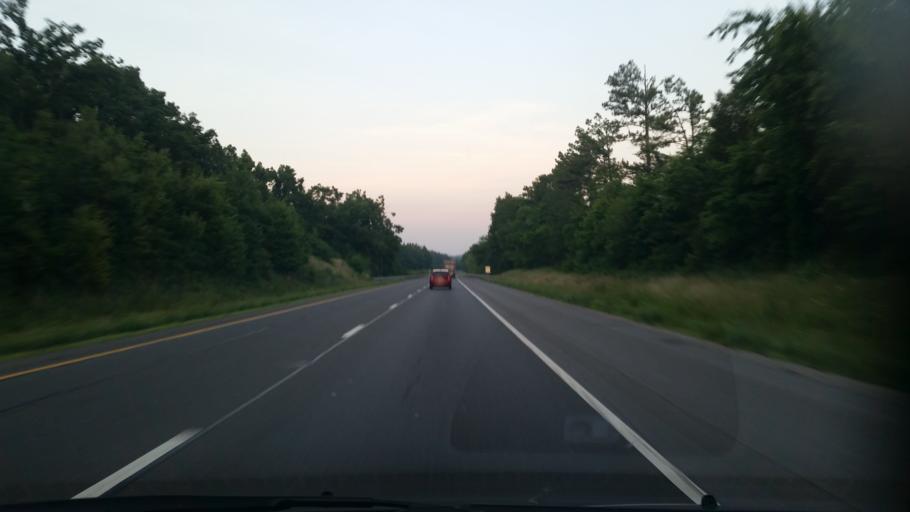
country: US
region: Tennessee
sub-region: Cumberland County
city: Crossville
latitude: 36.0453
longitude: -85.1281
